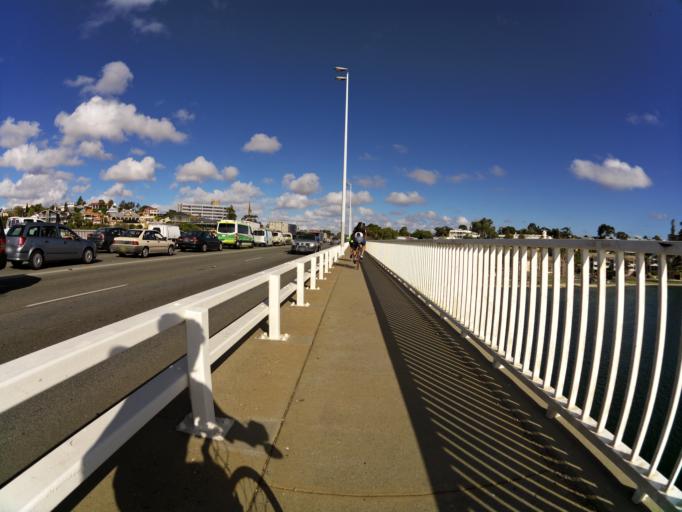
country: AU
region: Western Australia
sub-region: East Fremantle
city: East Fremantle
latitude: -32.0397
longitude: 115.7598
